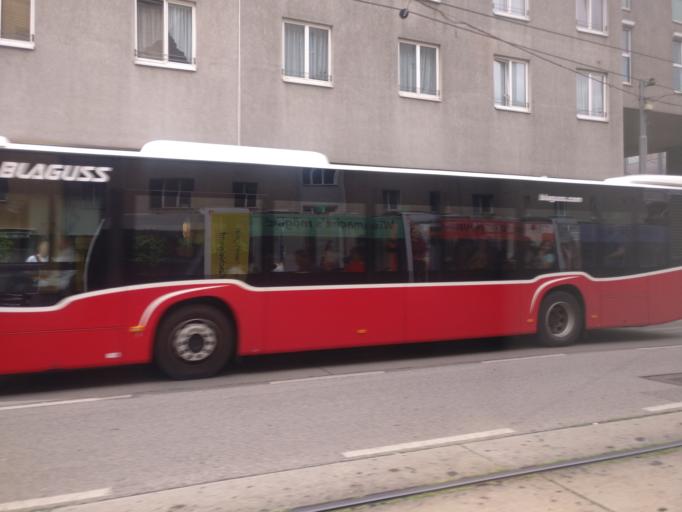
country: AT
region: Vienna
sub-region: Wien Stadt
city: Vienna
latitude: 48.2358
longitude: 16.3703
